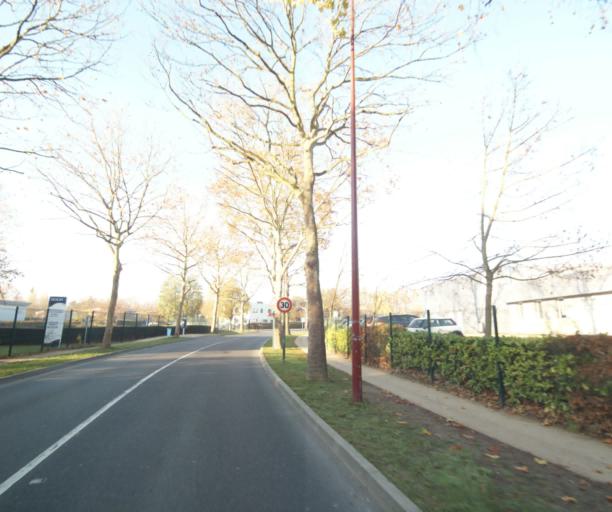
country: FR
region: Ile-de-France
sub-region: Departement du Val-d'Oise
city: Gonesse
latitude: 48.9904
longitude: 2.4366
